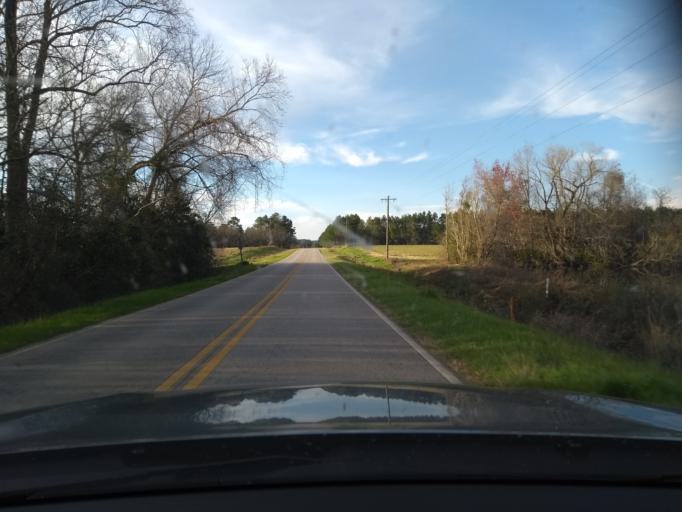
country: US
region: Georgia
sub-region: Bulloch County
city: Brooklet
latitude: 32.3082
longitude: -81.7750
